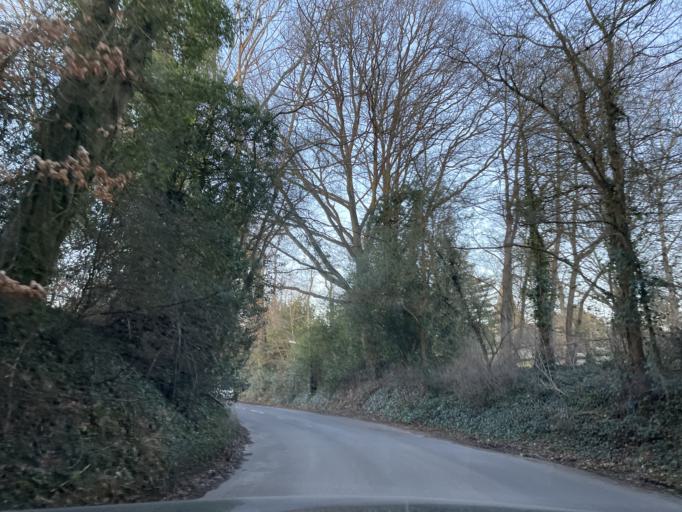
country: GB
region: England
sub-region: Kent
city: Halstead
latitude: 51.2732
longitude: 0.1272
